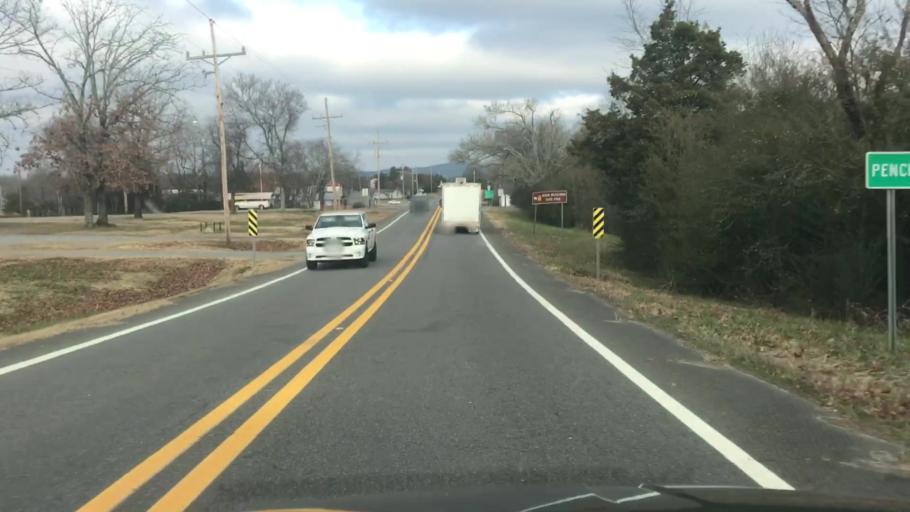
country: US
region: Arkansas
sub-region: Montgomery County
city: Mount Ida
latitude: 34.6274
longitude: -93.7320
